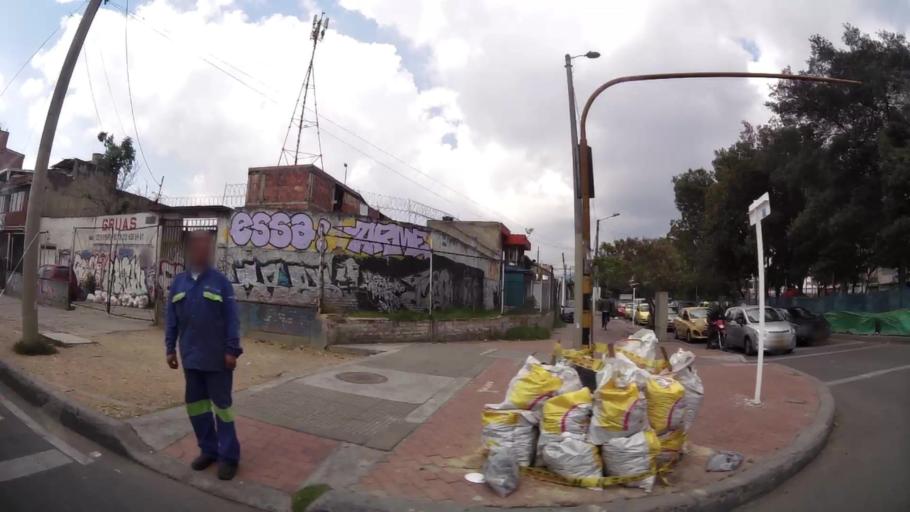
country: CO
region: Bogota D.C.
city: Bogota
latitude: 4.5797
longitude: -74.0999
